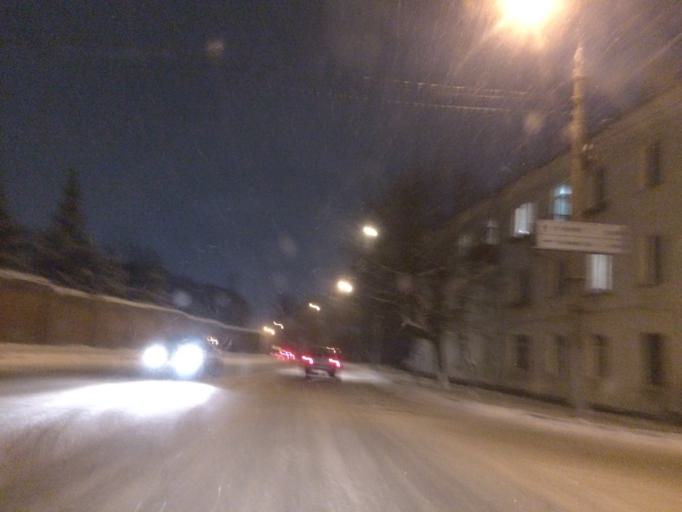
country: RU
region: Tula
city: Tula
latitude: 54.1760
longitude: 37.6127
